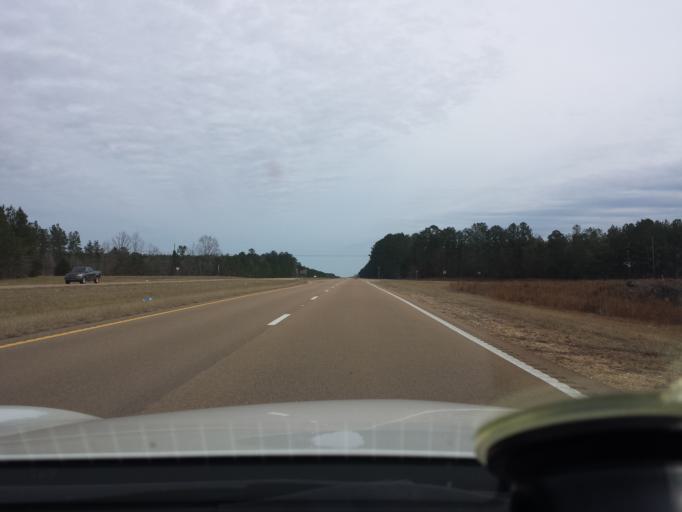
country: US
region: Mississippi
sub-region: Rankin County
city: Pelahatchie
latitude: 32.5459
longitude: -89.7920
